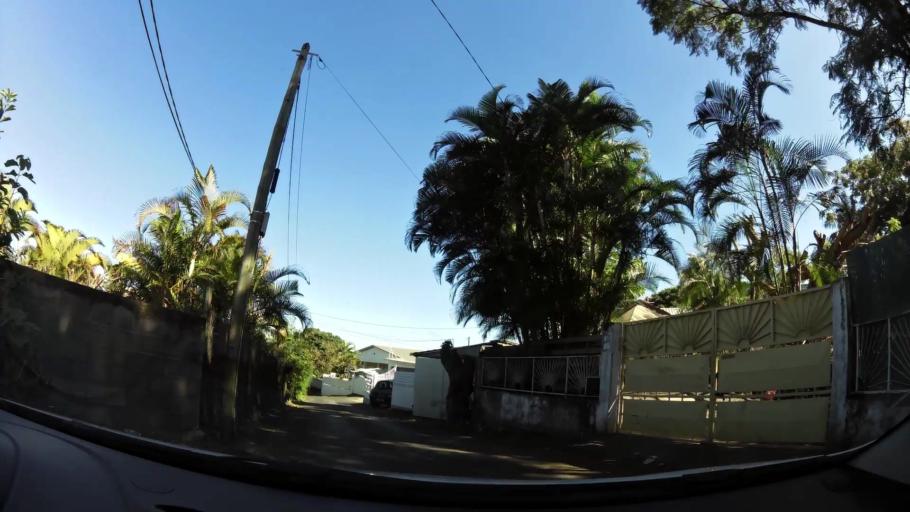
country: RE
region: Reunion
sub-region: Reunion
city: Le Tampon
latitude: -21.2619
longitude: 55.5037
